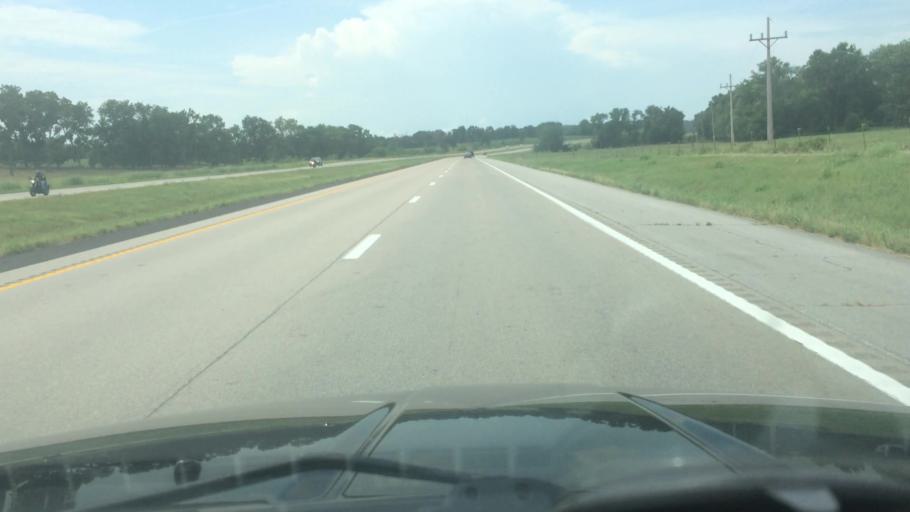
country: US
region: Missouri
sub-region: Polk County
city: Humansville
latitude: 37.8182
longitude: -93.6119
